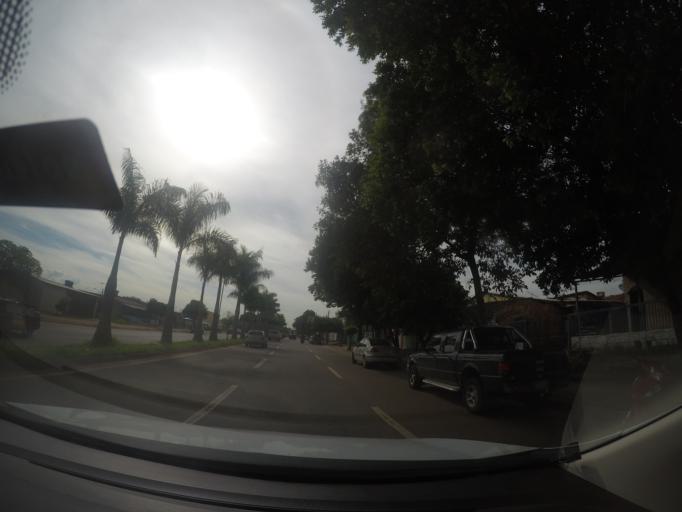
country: BR
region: Goias
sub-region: Goiania
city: Goiania
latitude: -16.6566
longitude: -49.2982
